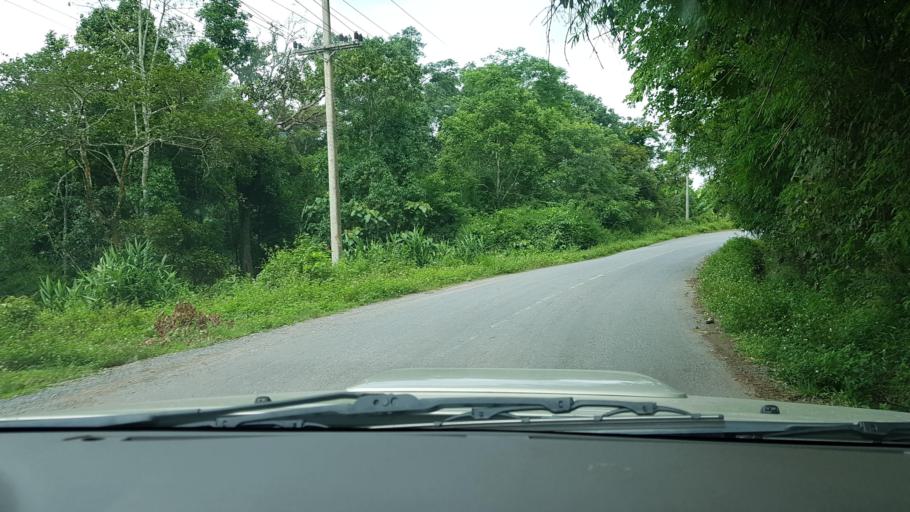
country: LA
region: Oudomxai
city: Muang Xay
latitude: 20.5949
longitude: 101.9384
